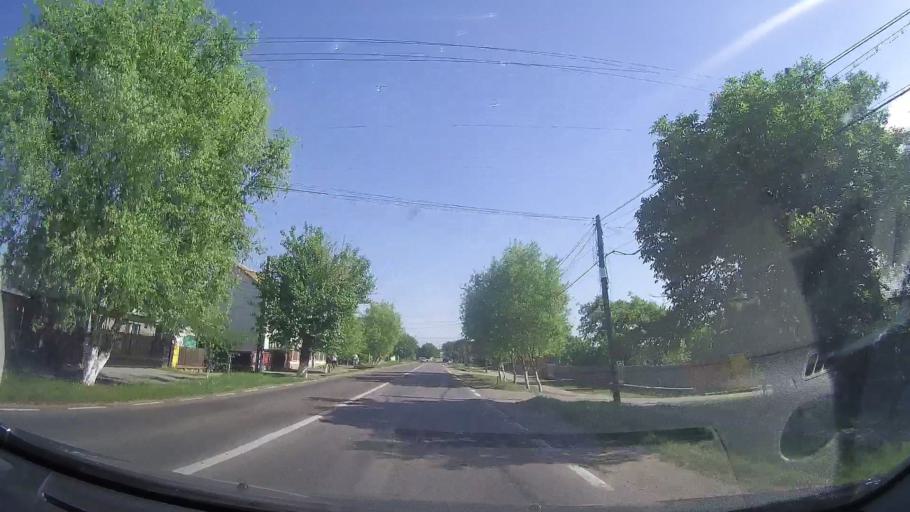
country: RO
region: Prahova
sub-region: Comuna Magurele
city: Magurele
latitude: 45.0990
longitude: 26.0364
